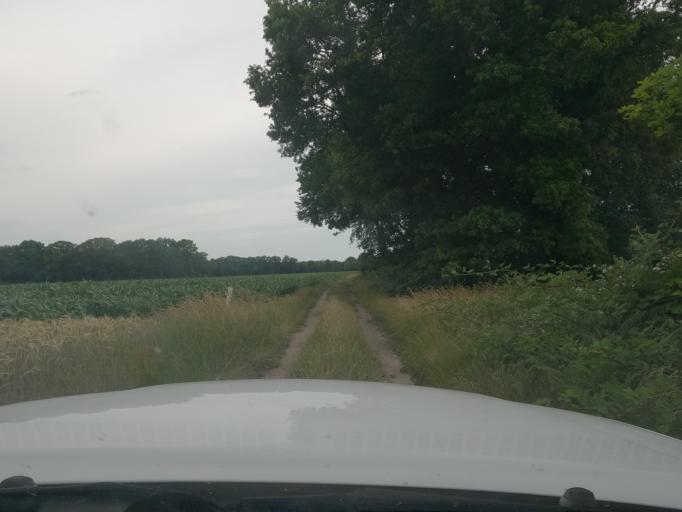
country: DE
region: North Rhine-Westphalia
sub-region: Regierungsbezirk Munster
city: Raesfeld
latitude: 51.7288
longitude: 6.8711
